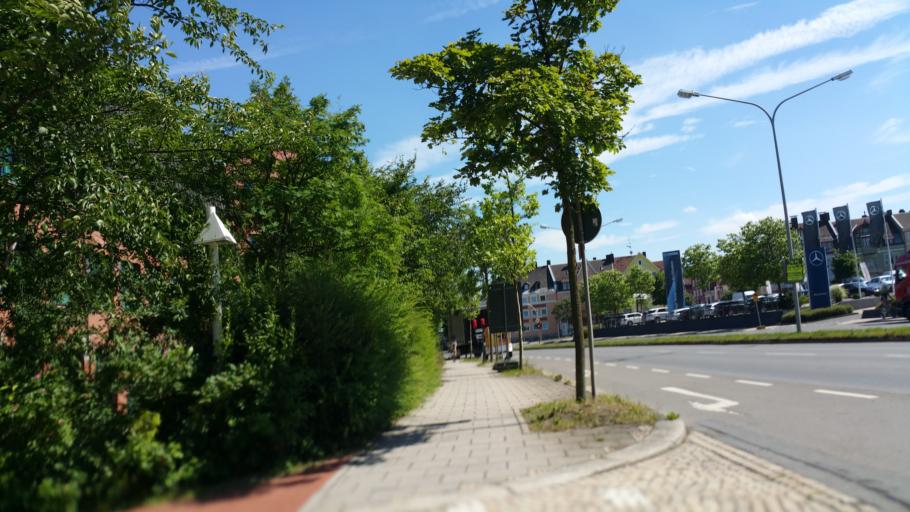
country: DE
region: Bavaria
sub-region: Upper Franconia
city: Hof
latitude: 50.3132
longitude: 11.9067
